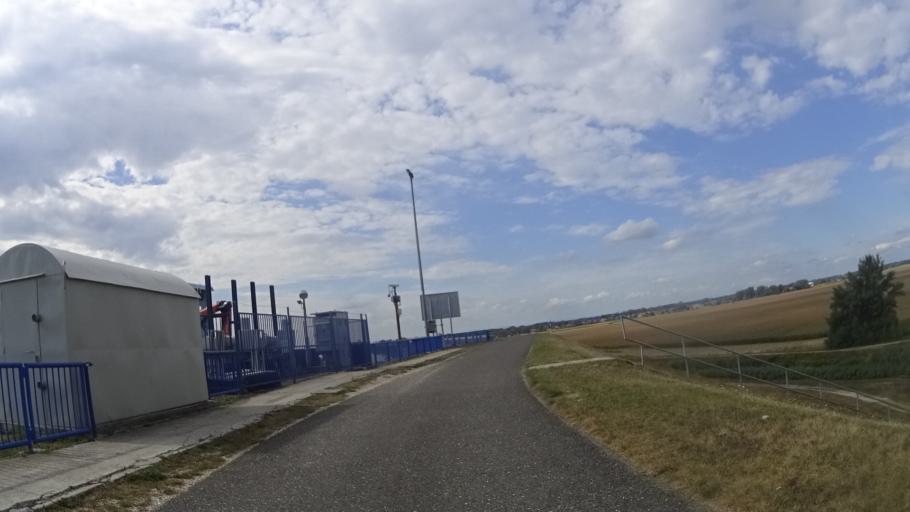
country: SK
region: Trnavsky
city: Gabcikovo
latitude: 47.8894
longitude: 17.5342
